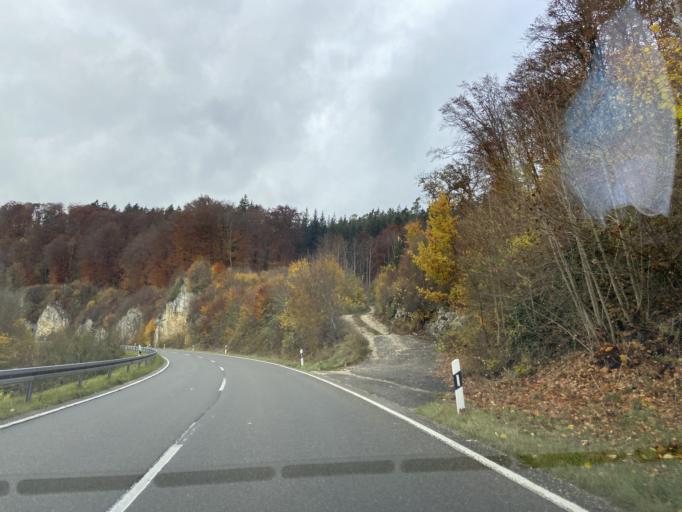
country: DE
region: Baden-Wuerttemberg
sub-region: Tuebingen Region
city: Inzigkofen
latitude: 48.0815
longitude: 9.1716
